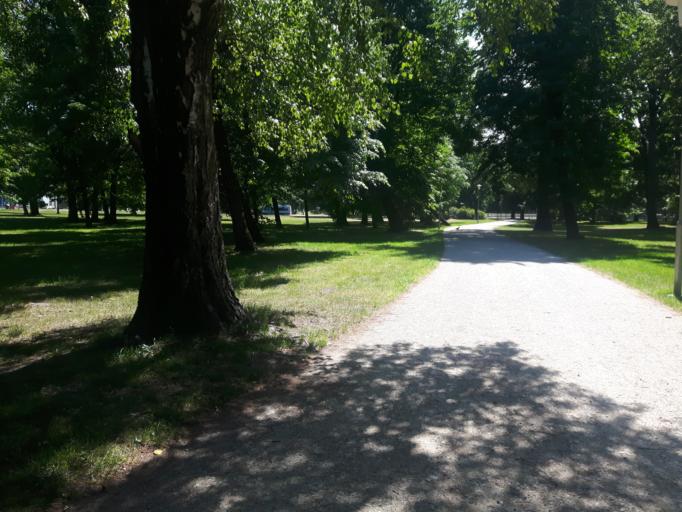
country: LV
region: Liepaja
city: Liepaja
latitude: 56.5185
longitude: 21.0196
